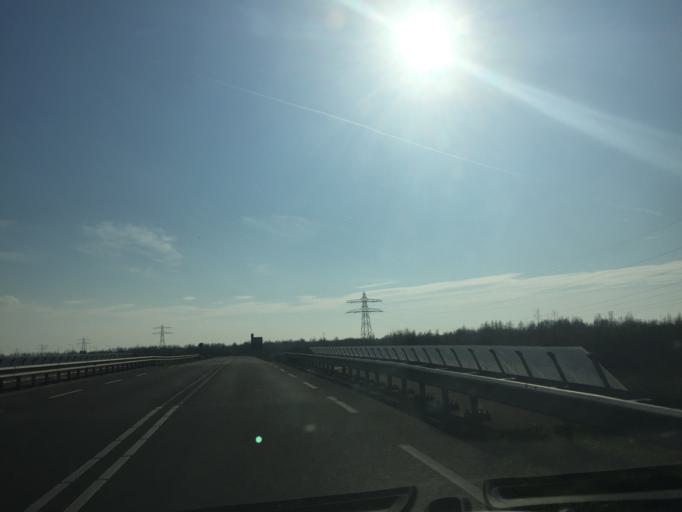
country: NL
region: South Holland
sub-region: Gemeente Hillegom
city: Hillegom
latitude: 52.2741
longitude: 4.5902
